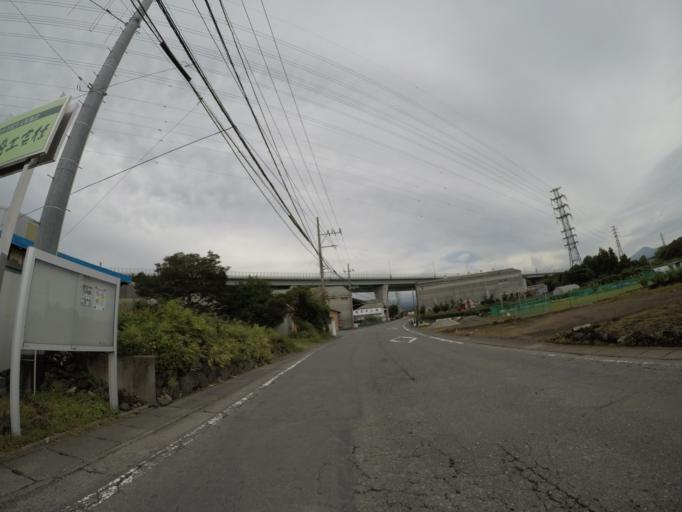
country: JP
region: Shizuoka
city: Fujinomiya
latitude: 35.1998
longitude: 138.6539
